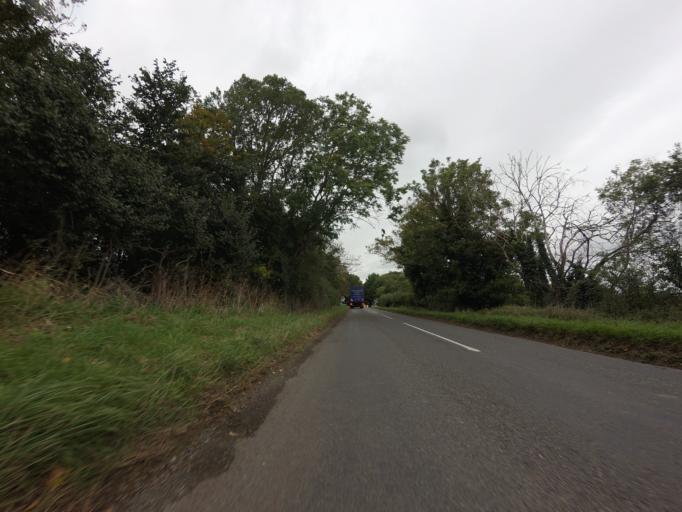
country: GB
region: England
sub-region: Cambridgeshire
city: Meldreth
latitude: 52.1074
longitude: 0.0442
